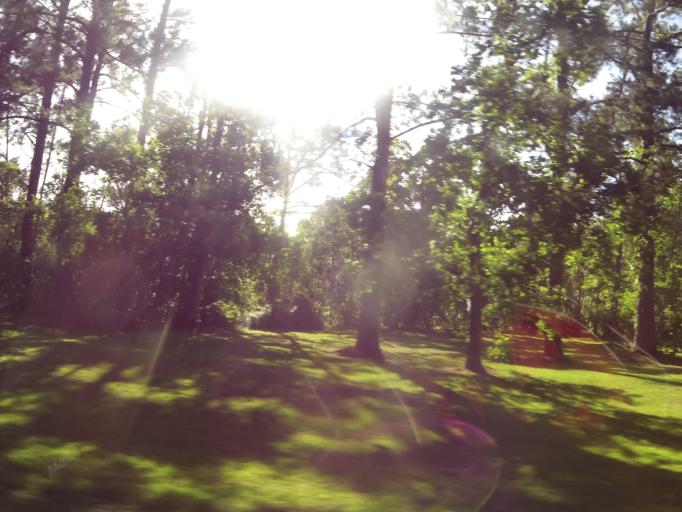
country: US
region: Florida
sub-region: Nassau County
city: Nassau Village-Ratliff
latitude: 30.5159
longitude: -81.7793
